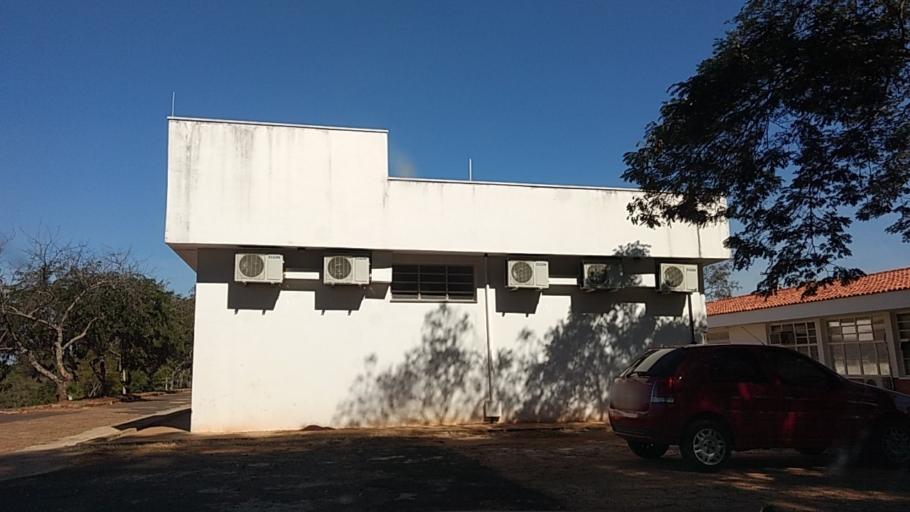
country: BR
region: Sao Paulo
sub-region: Botucatu
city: Botucatu
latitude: -22.8497
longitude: -48.4328
